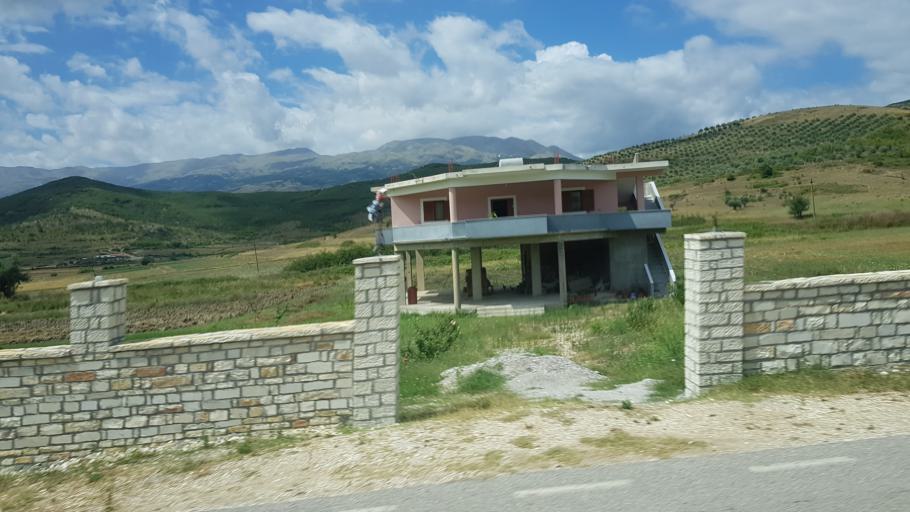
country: AL
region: Gjirokaster
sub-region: Rrethi i Tepelenes
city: Krahes
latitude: 40.4243
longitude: 19.8554
